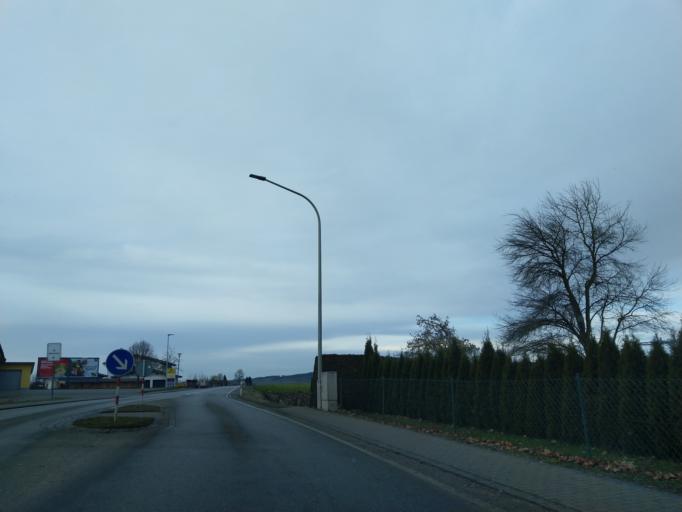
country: DE
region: Bavaria
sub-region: Lower Bavaria
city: Rossbach
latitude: 48.6197
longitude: 12.9798
